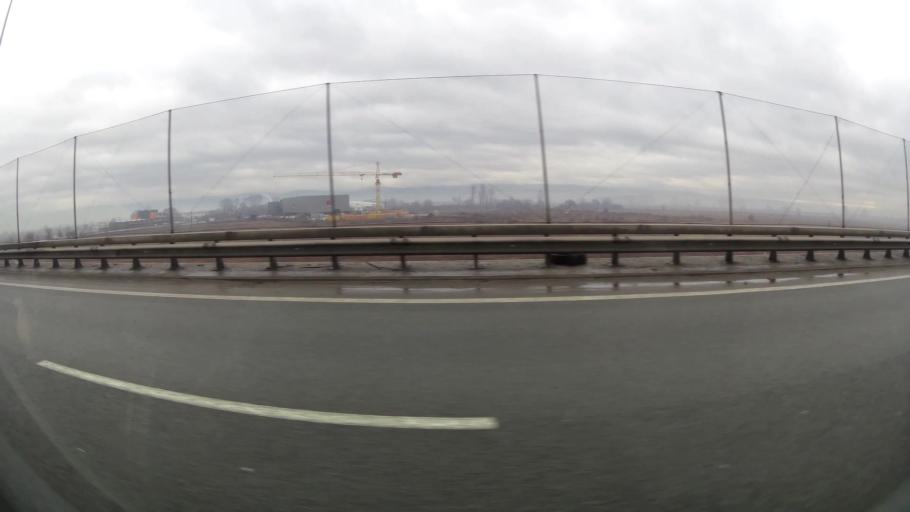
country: BG
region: Sofia-Capital
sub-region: Stolichna Obshtina
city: Sofia
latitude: 42.7112
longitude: 23.4351
